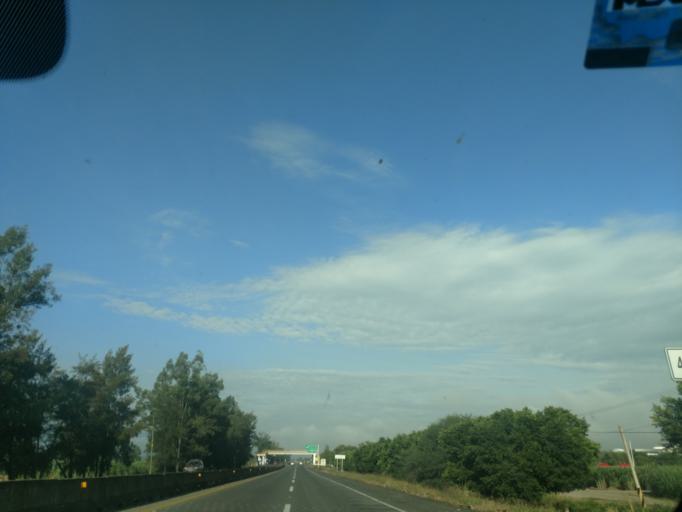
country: MX
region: Jalisco
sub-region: Ameca
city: Los Pocitos
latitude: 20.5346
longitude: -103.9636
